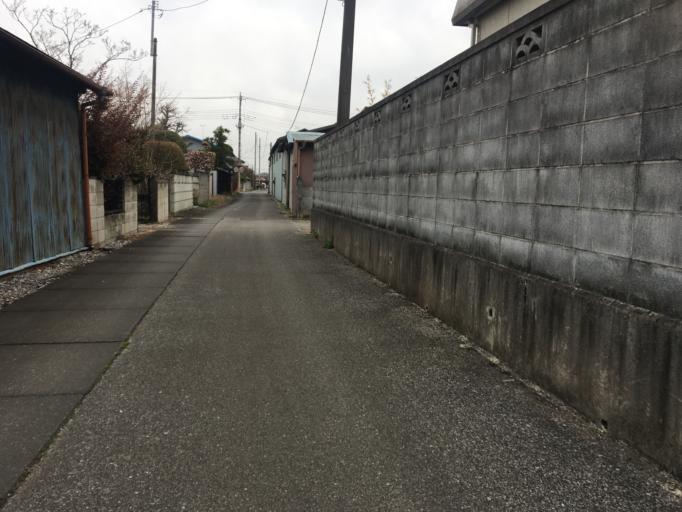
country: JP
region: Saitama
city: Kisai
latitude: 36.1034
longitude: 139.5734
